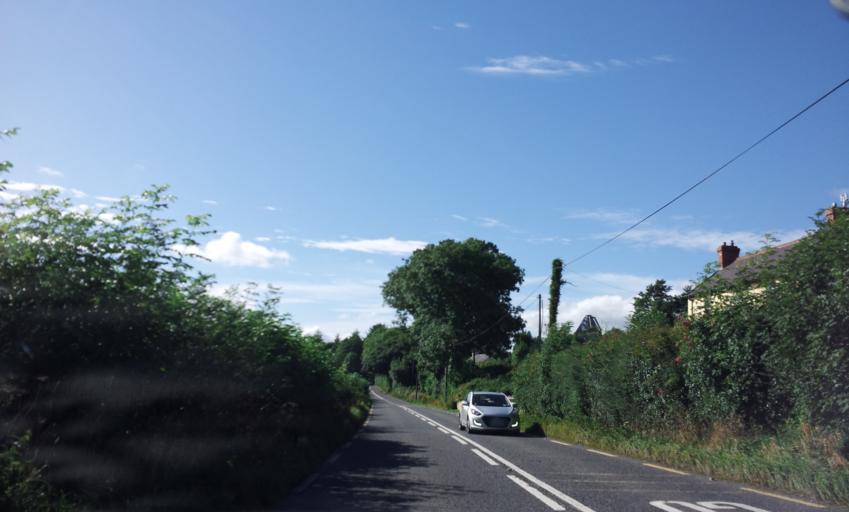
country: IE
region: Munster
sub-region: County Cork
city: Millstreet
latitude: 51.9239
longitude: -9.0974
